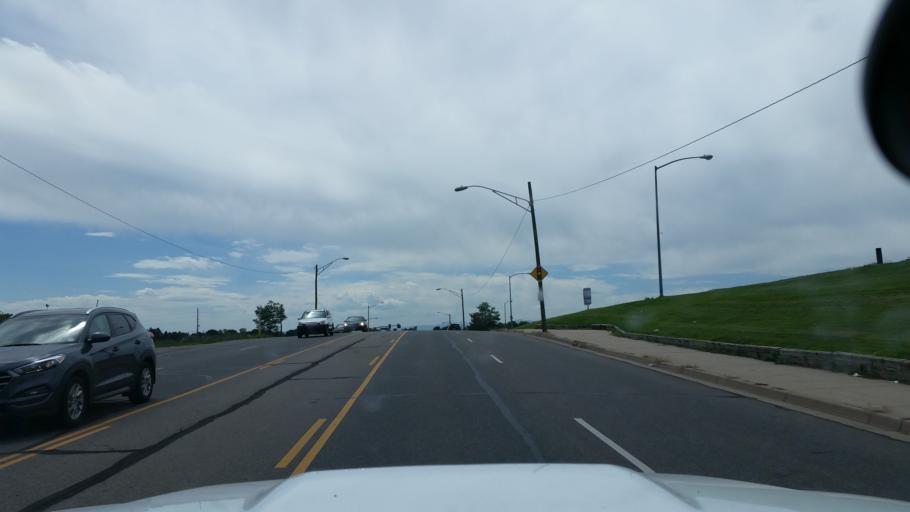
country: US
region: Colorado
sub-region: Adams County
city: Federal Heights
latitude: 39.8585
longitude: -105.0060
